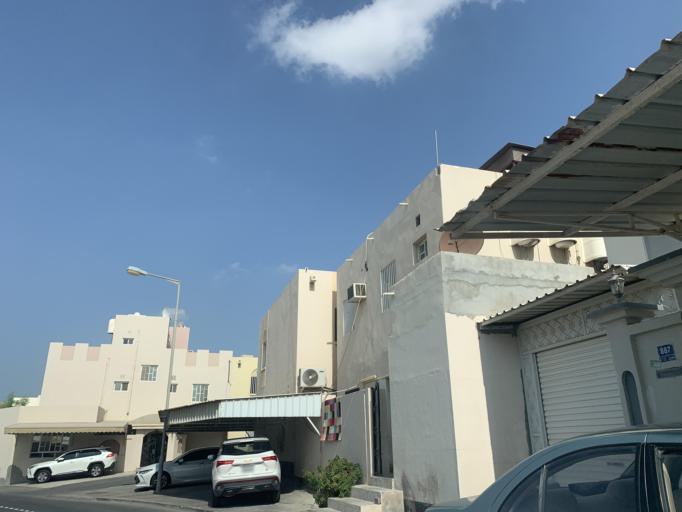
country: BH
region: Central Governorate
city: Madinat Hamad
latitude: 26.1381
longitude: 50.5019
